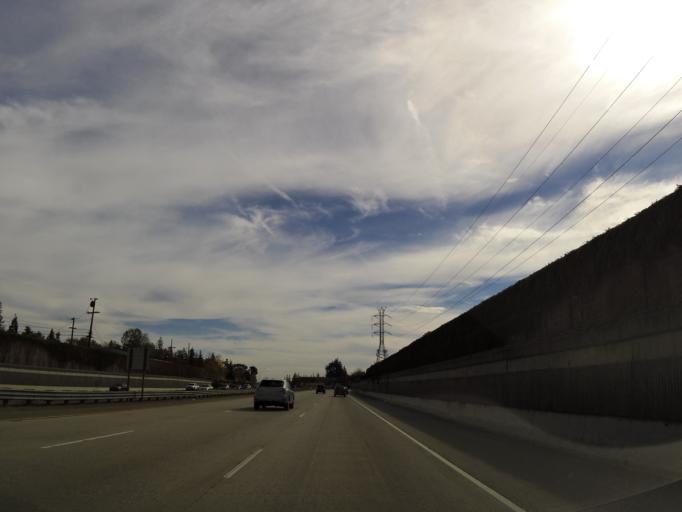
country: US
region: California
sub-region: Santa Clara County
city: Monte Sereno
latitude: 37.2613
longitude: -121.9727
